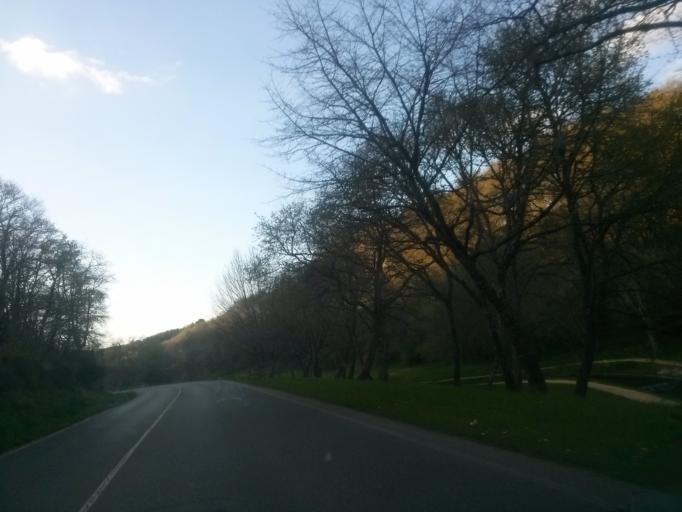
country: ES
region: Galicia
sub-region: Provincia de Lugo
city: Lugo
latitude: 43.0008
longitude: -7.5319
